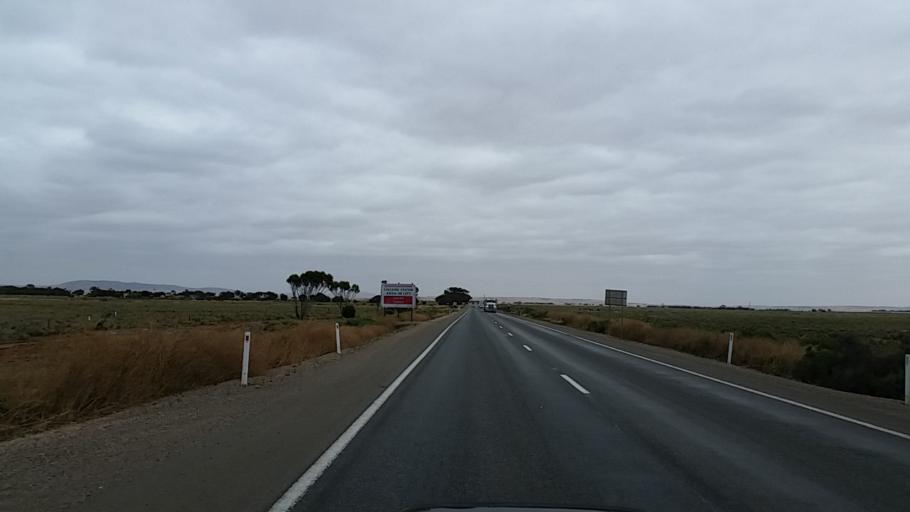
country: AU
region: South Australia
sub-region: Wakefield
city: Balaklava
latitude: -34.1761
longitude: 138.1543
